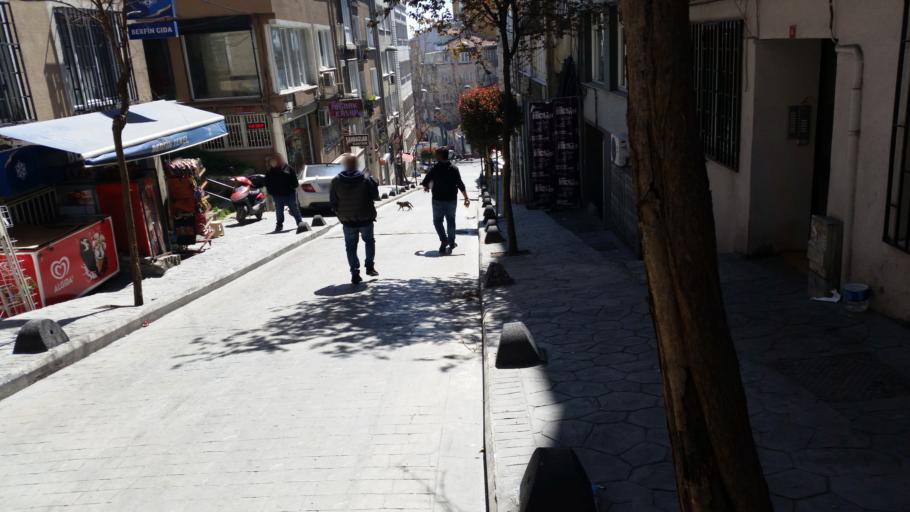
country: TR
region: Istanbul
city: Eminoenue
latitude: 41.0343
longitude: 28.9867
